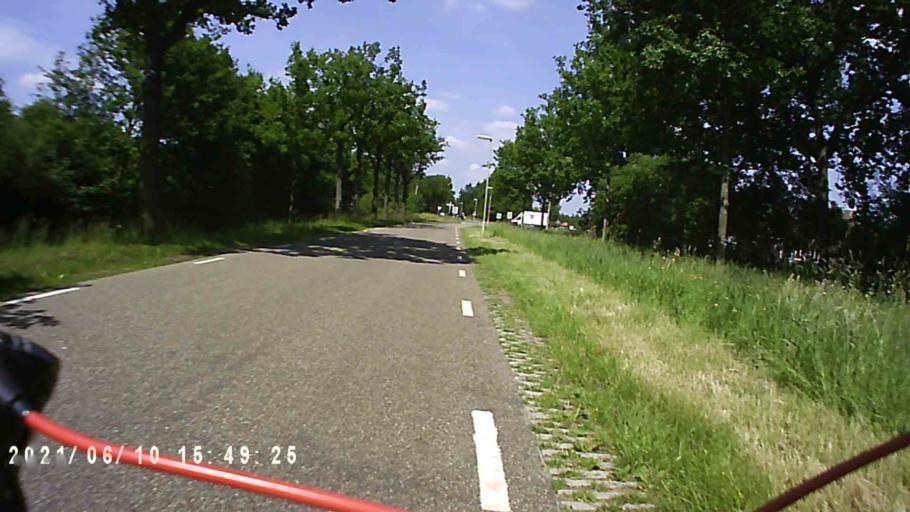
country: NL
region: Friesland
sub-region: Gemeente Achtkarspelen
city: Harkema
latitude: 53.1682
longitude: 6.1195
